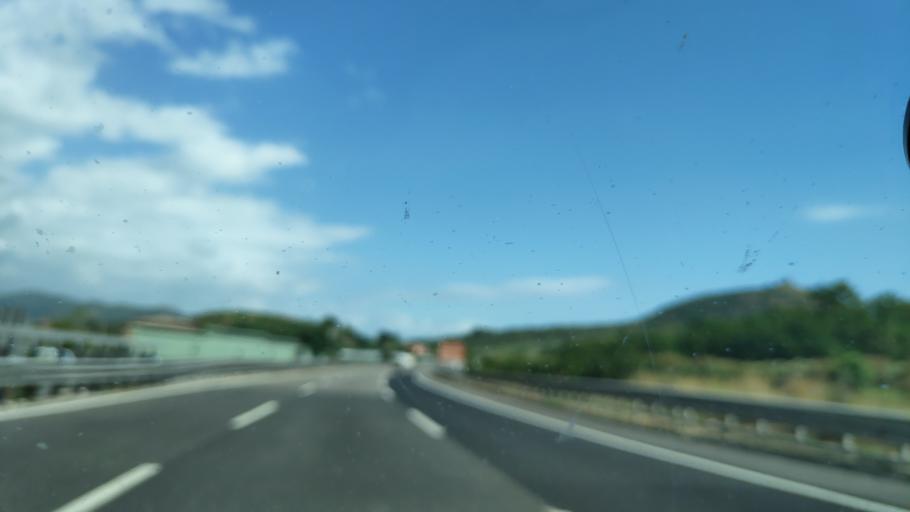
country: IT
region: Campania
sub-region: Provincia di Salerno
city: San Mango Piemonte
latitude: 40.6855
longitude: 14.8517
